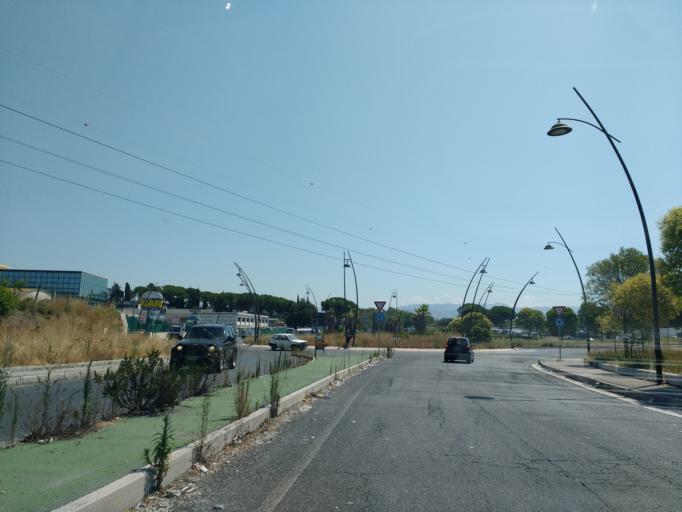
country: IT
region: Latium
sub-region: Citta metropolitana di Roma Capitale
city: Setteville
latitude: 41.9471
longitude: 12.6714
